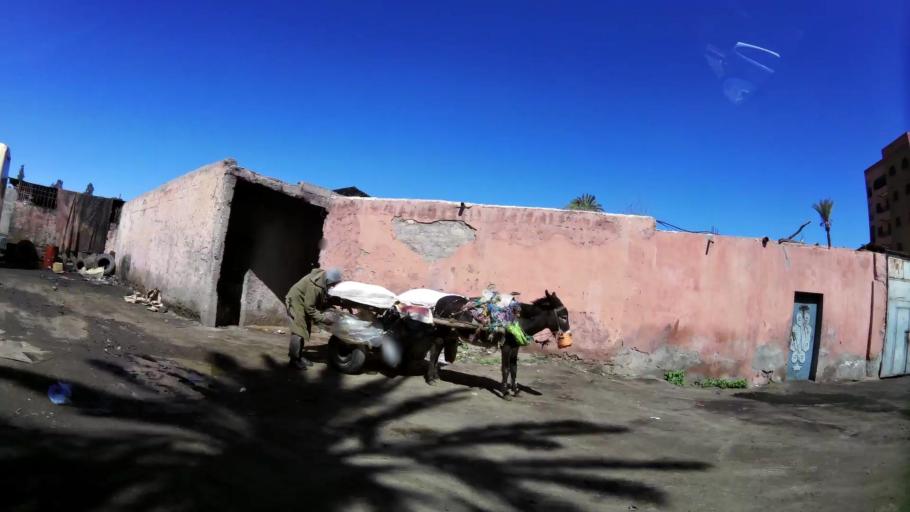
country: MA
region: Marrakech-Tensift-Al Haouz
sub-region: Marrakech
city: Marrakesh
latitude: 31.6367
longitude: -8.0031
